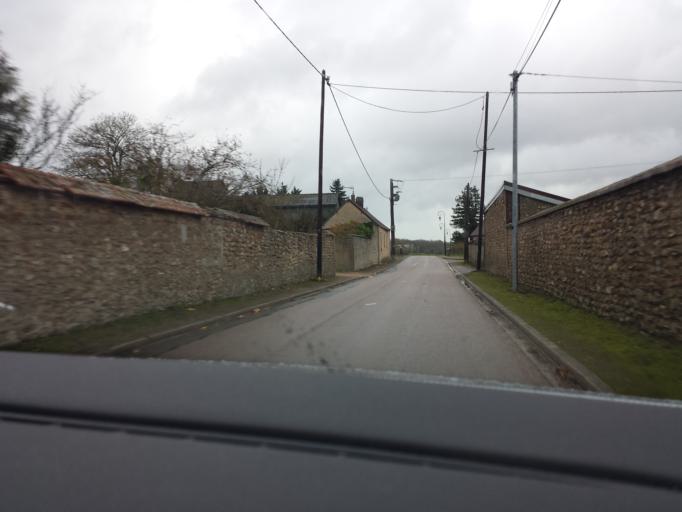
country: FR
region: Haute-Normandie
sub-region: Departement de l'Eure
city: Evreux
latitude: 49.0058
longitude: 1.1965
